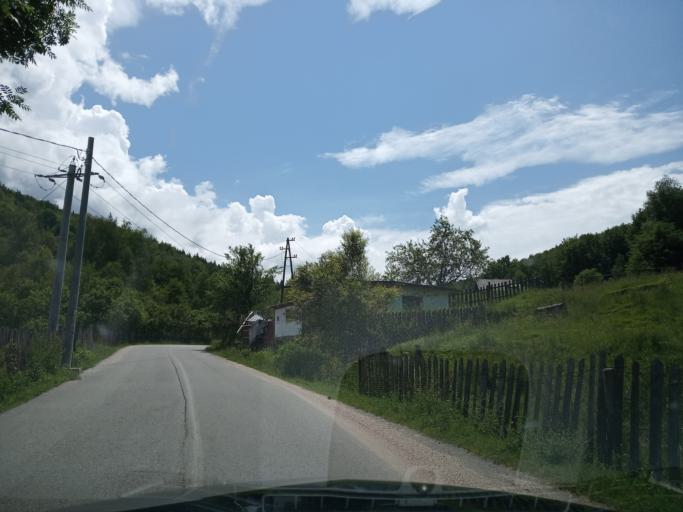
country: RO
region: Hunedoara
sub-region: Oras Petrila
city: Petrila
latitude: 45.4021
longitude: 23.4145
